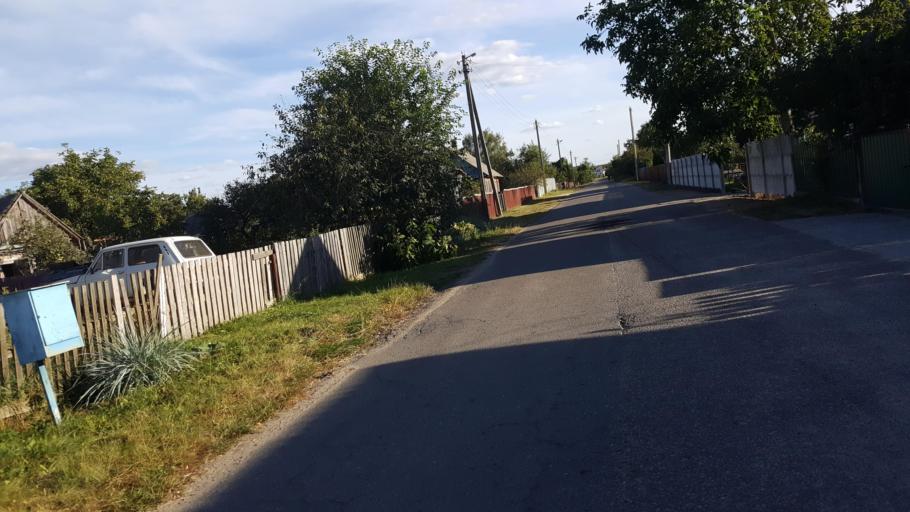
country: BY
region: Brest
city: Kamyanyets
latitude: 52.3989
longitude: 23.8155
